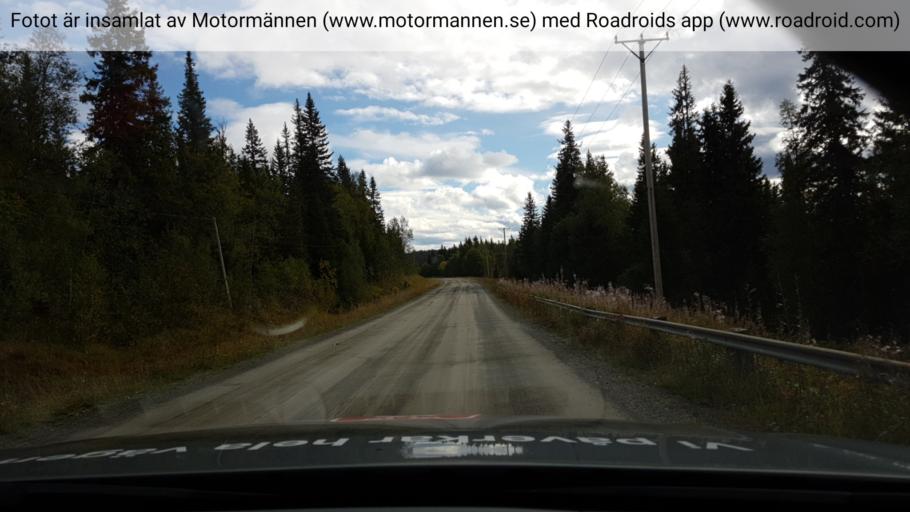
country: SE
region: Jaemtland
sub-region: Are Kommun
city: Are
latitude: 63.6931
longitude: 12.7991
